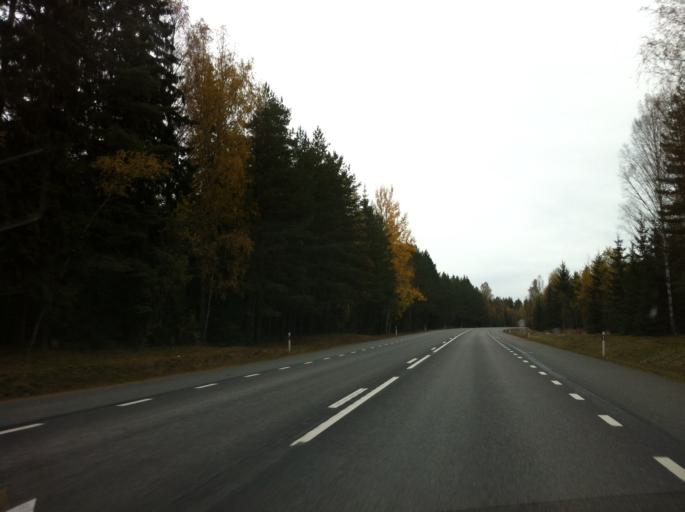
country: SE
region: OErebro
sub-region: Lindesbergs Kommun
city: Stora
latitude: 59.7681
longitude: 15.1482
